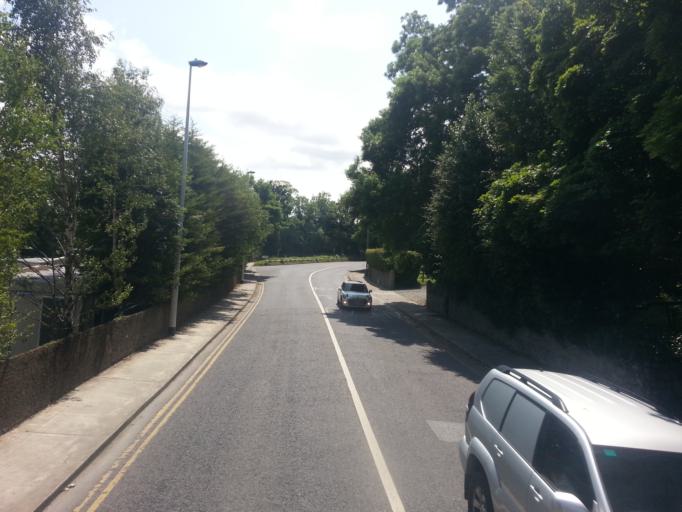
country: IE
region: Leinster
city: Foxrock
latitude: 53.2455
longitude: -6.1997
